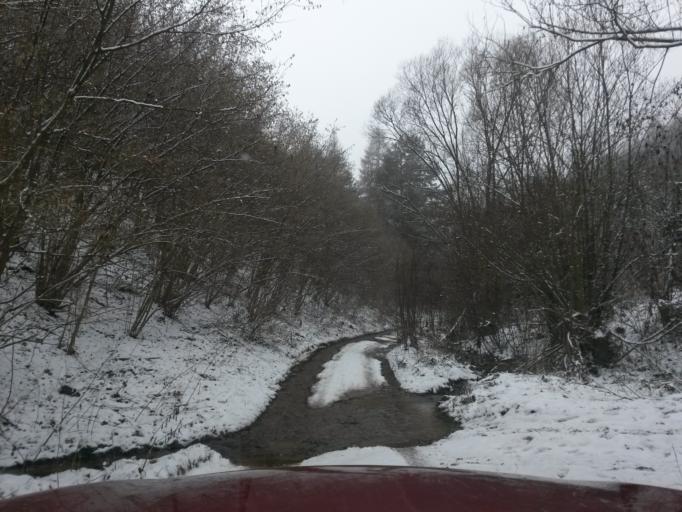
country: SK
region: Kosicky
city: Krompachy
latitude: 48.9833
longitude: 20.9894
